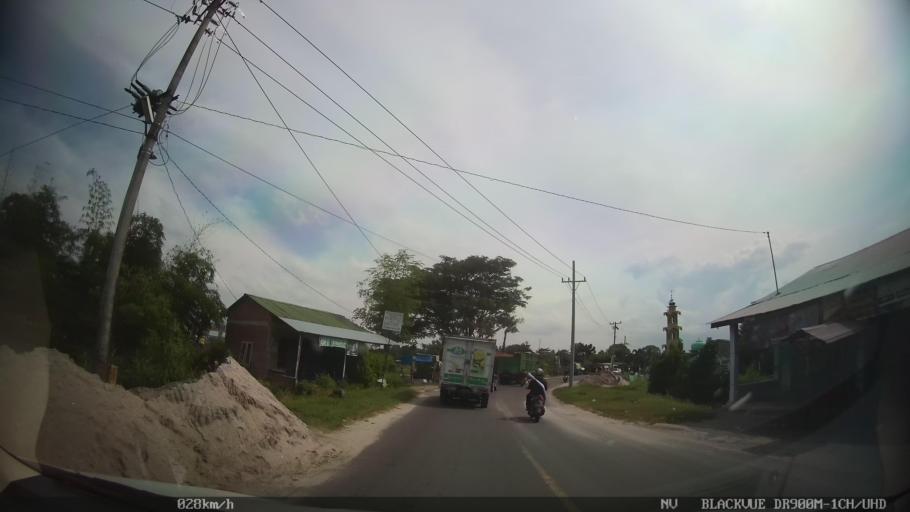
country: ID
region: North Sumatra
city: Percut
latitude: 3.6161
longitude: 98.8334
